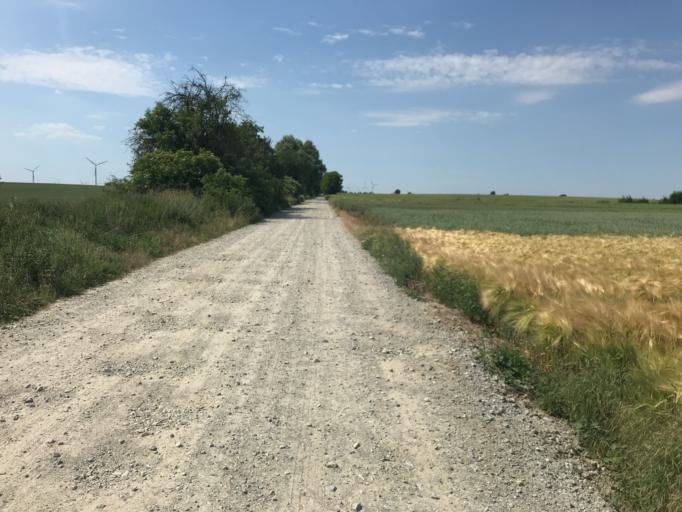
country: PL
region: West Pomeranian Voivodeship
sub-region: Powiat mysliborski
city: Boleszkowice
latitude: 52.7124
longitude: 14.6354
